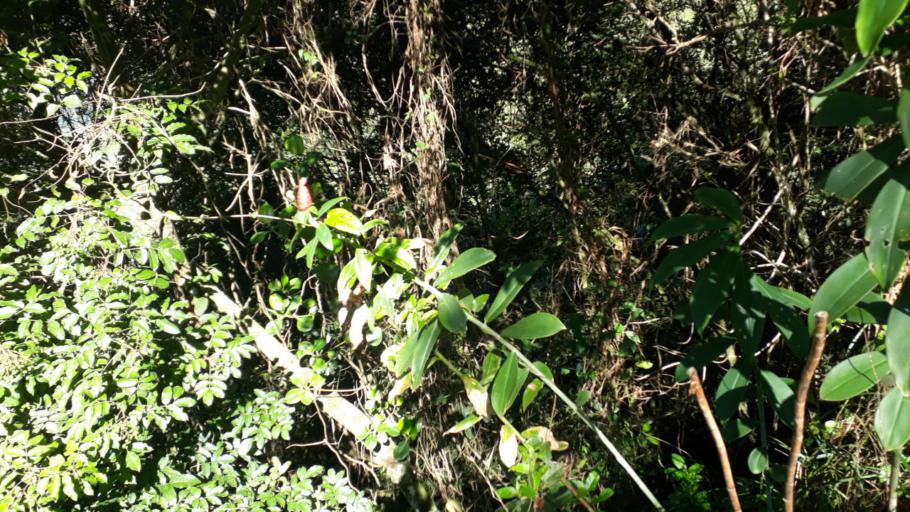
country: CO
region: Casanare
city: Nunchia
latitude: 5.6530
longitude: -72.4231
